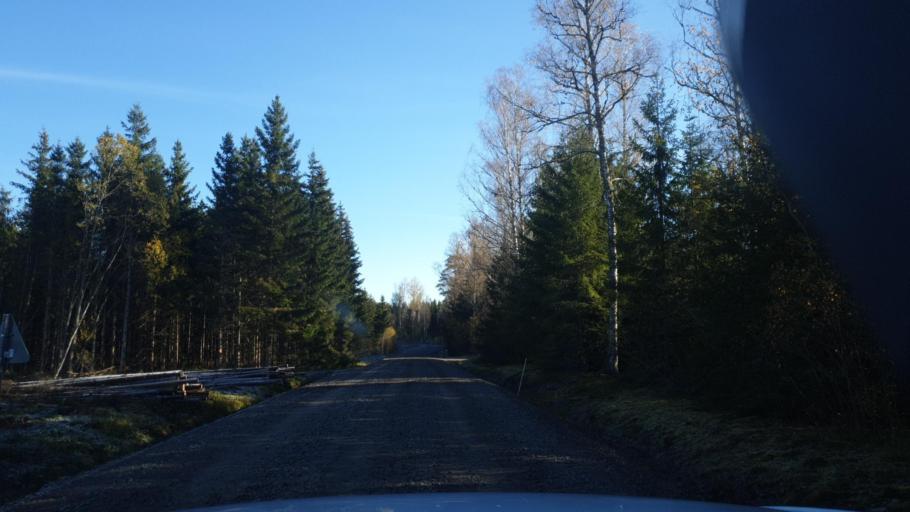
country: SE
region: Vaermland
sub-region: Grums Kommun
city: Grums
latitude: 59.4220
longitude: 13.0911
